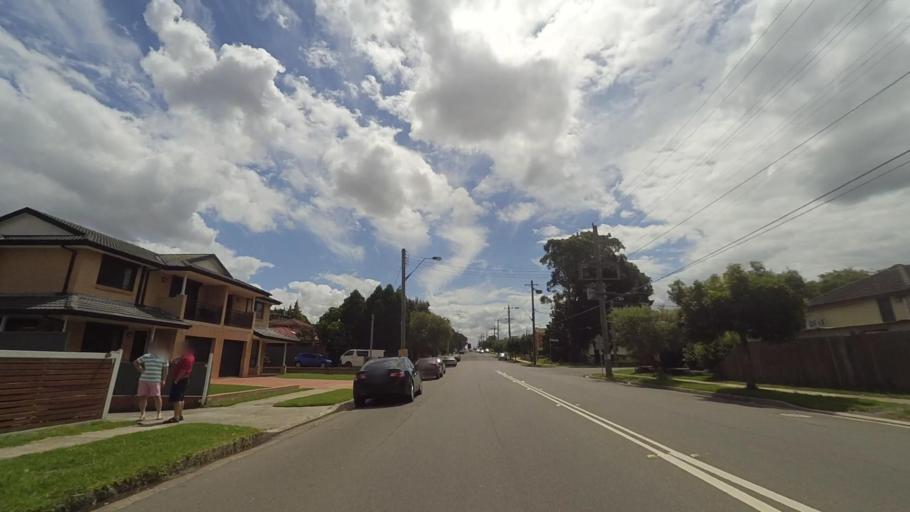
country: AU
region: New South Wales
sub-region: Fairfield
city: Fairfield Heights
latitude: -33.8626
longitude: 150.9436
